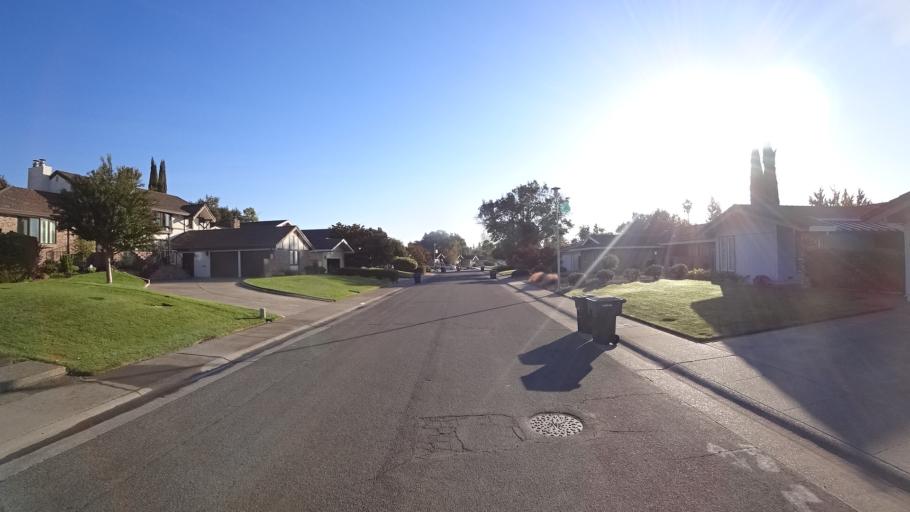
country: US
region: California
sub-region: Yolo County
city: West Sacramento
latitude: 38.5155
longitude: -121.5378
